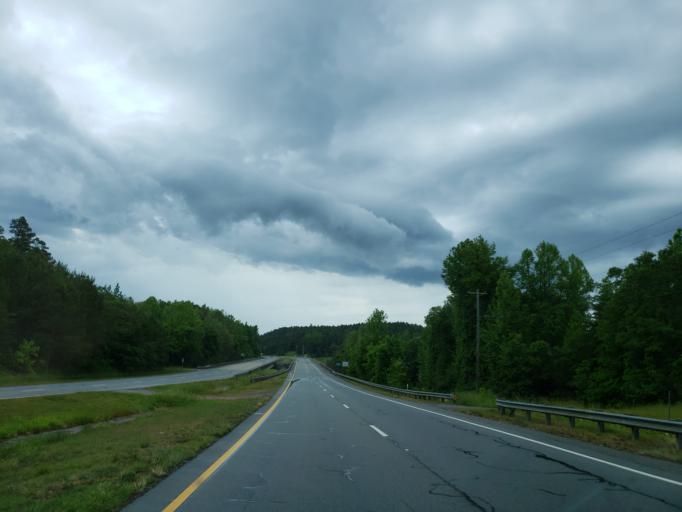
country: US
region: Georgia
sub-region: Haralson County
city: Buchanan
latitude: 33.8651
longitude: -85.2141
